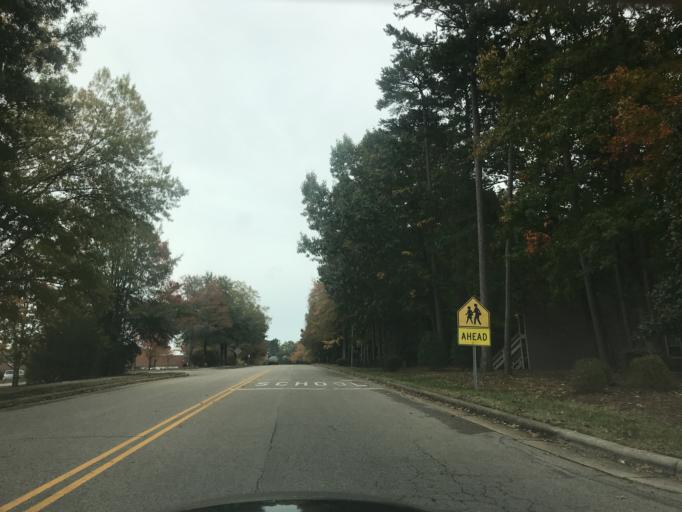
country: US
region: North Carolina
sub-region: Wake County
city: West Raleigh
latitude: 35.8972
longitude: -78.6558
